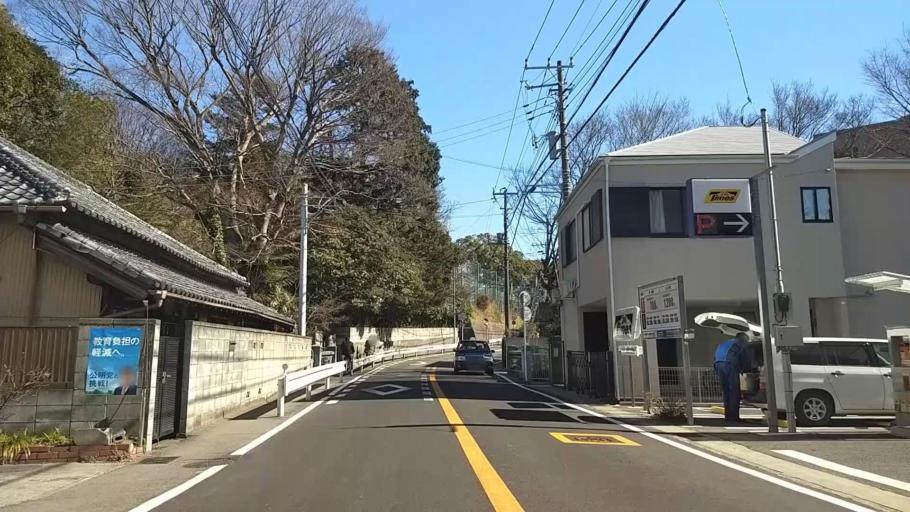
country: JP
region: Kanagawa
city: Kamakura
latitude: 35.3228
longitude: 139.5644
